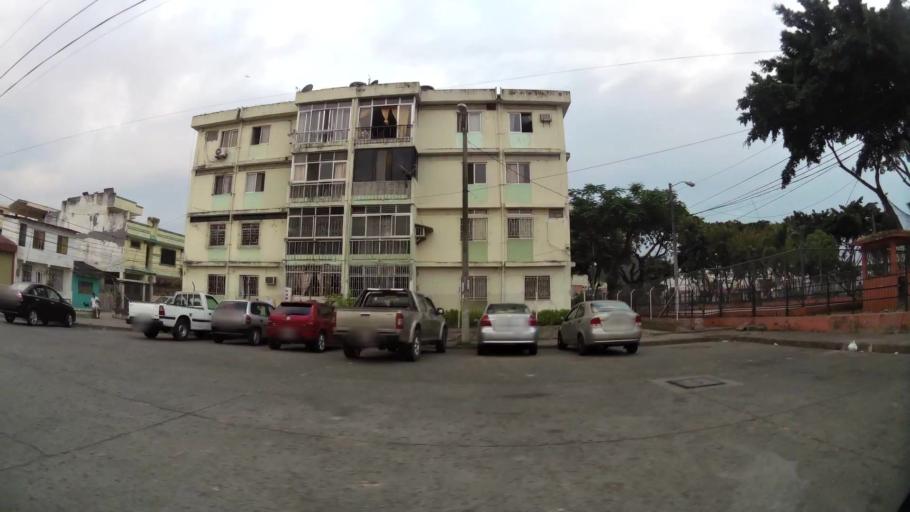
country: EC
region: Guayas
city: Eloy Alfaro
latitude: -2.1718
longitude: -79.8814
